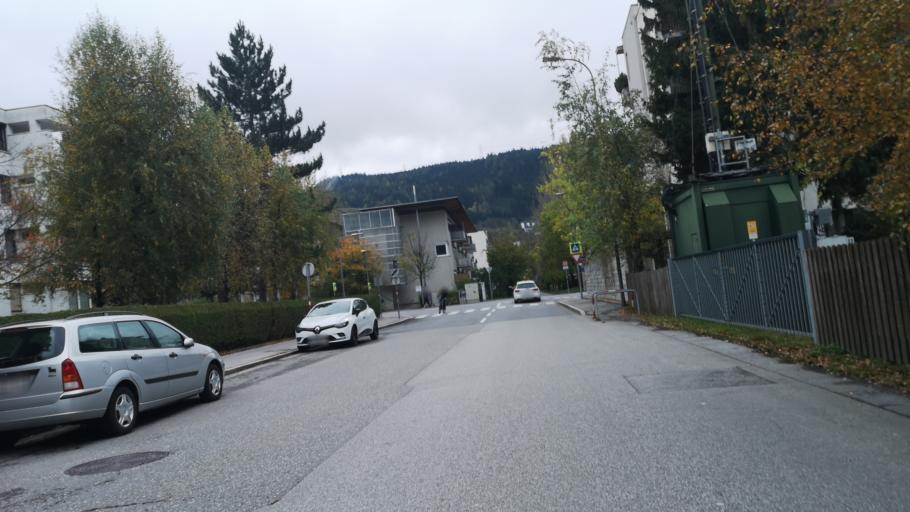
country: AT
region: Tyrol
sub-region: Politischer Bezirk Innsbruck Land
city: Natters
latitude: 47.2584
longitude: 11.3697
